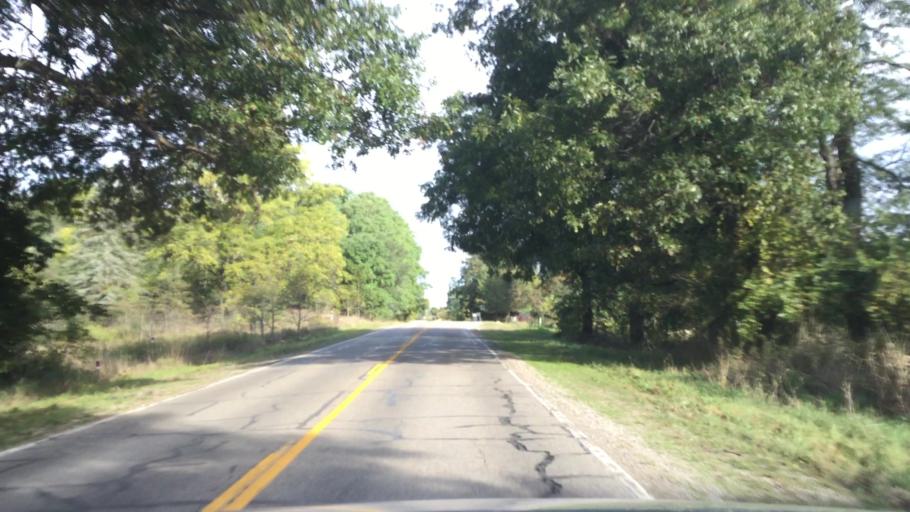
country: US
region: Michigan
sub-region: Livingston County
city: Howell
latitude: 42.5507
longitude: -83.8818
